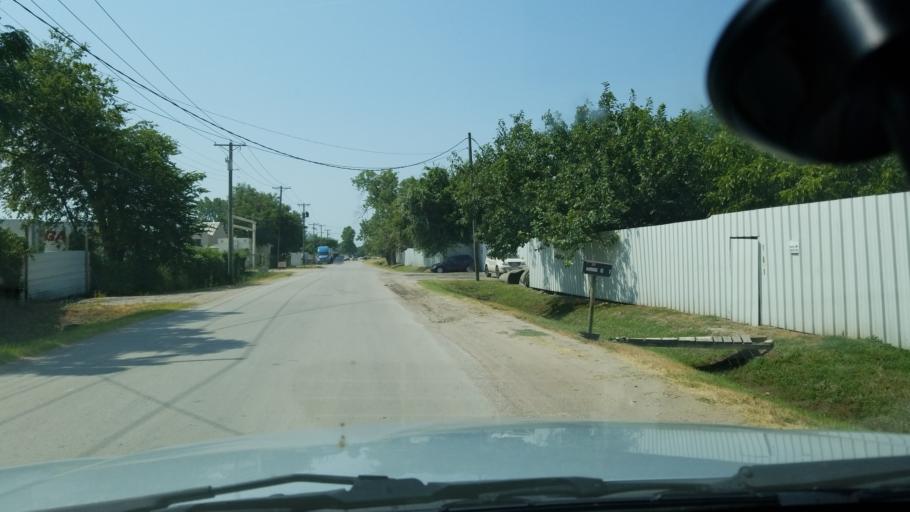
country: US
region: Texas
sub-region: Dallas County
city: Farmers Branch
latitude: 32.8705
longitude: -96.9024
